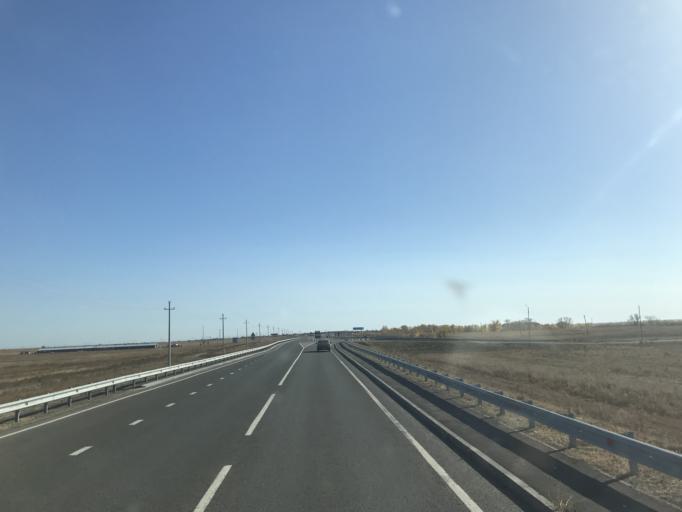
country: KZ
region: Pavlodar
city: Pavlodar
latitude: 52.1231
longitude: 77.0829
